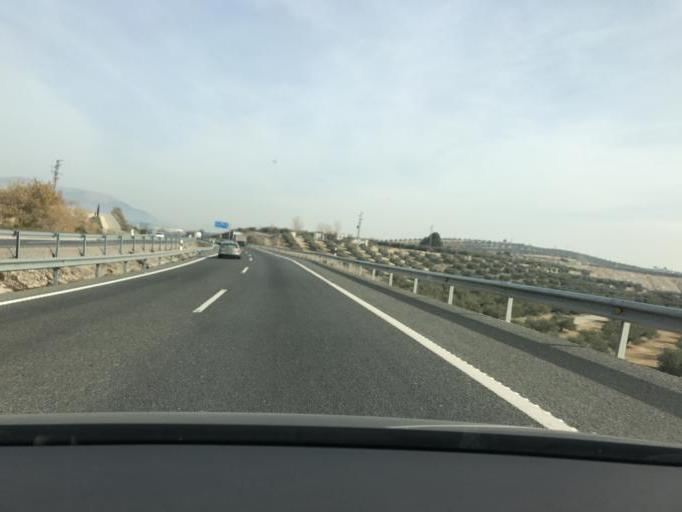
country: ES
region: Andalusia
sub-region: Provincia de Granada
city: Huetor-Tajar
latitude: 37.1830
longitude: -4.0357
